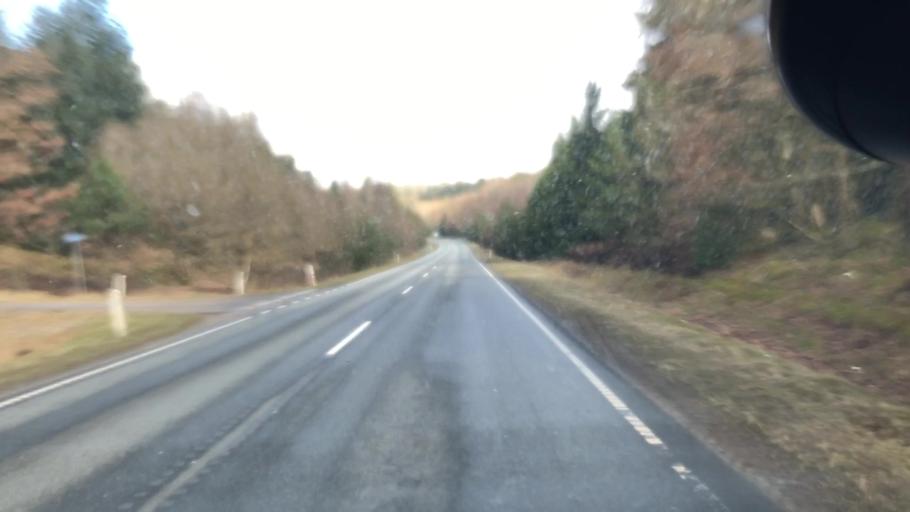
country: DK
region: Central Jutland
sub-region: Silkeborg Kommune
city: Virklund
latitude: 56.0655
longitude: 9.5800
